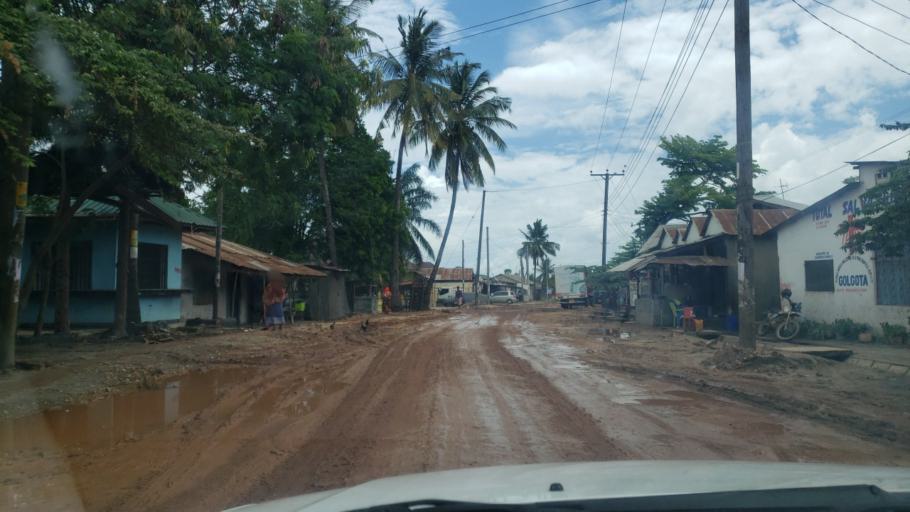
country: TZ
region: Dar es Salaam
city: Magomeni
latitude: -6.8071
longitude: 39.2326
